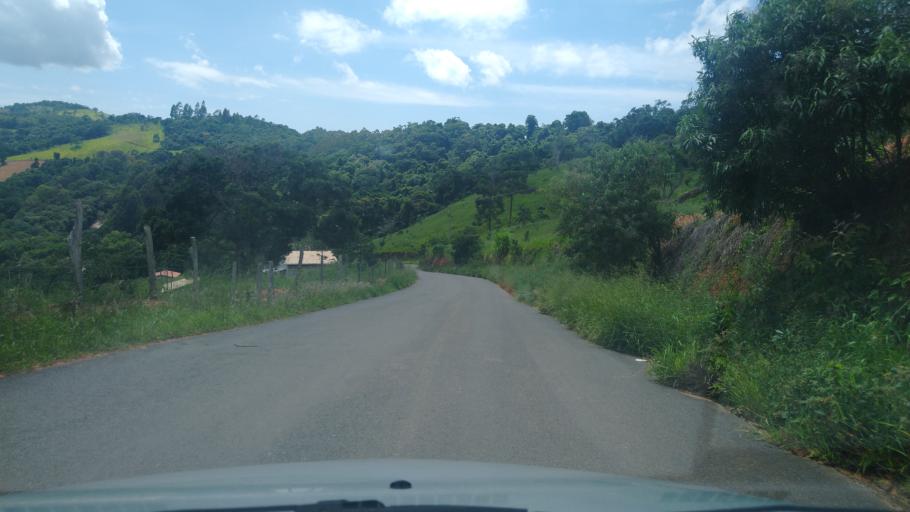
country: BR
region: Minas Gerais
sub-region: Extrema
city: Extrema
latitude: -22.7191
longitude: -46.3328
